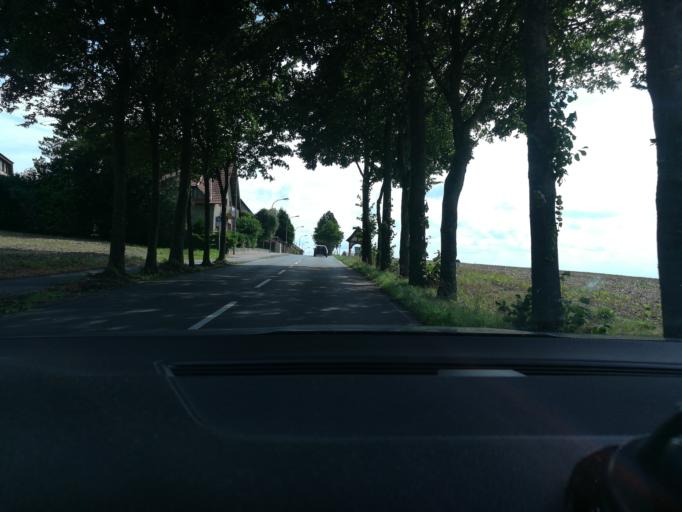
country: DE
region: North Rhine-Westphalia
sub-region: Regierungsbezirk Detmold
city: Huellhorst
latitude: 52.2849
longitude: 8.6880
